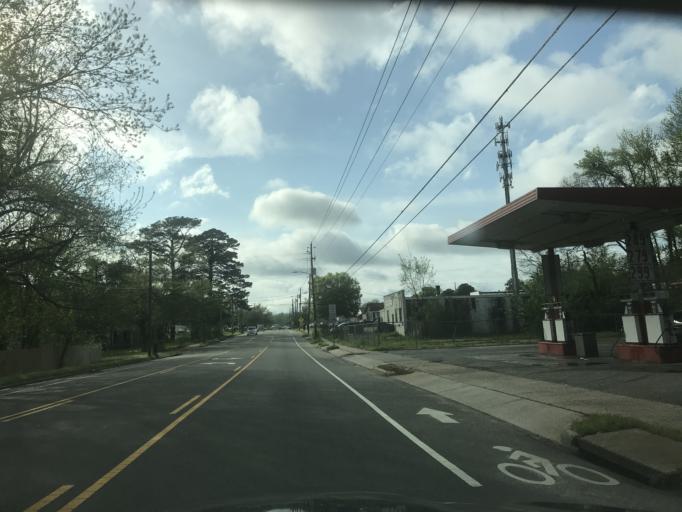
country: US
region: North Carolina
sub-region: Wake County
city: Raleigh
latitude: 35.7757
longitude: -78.6084
